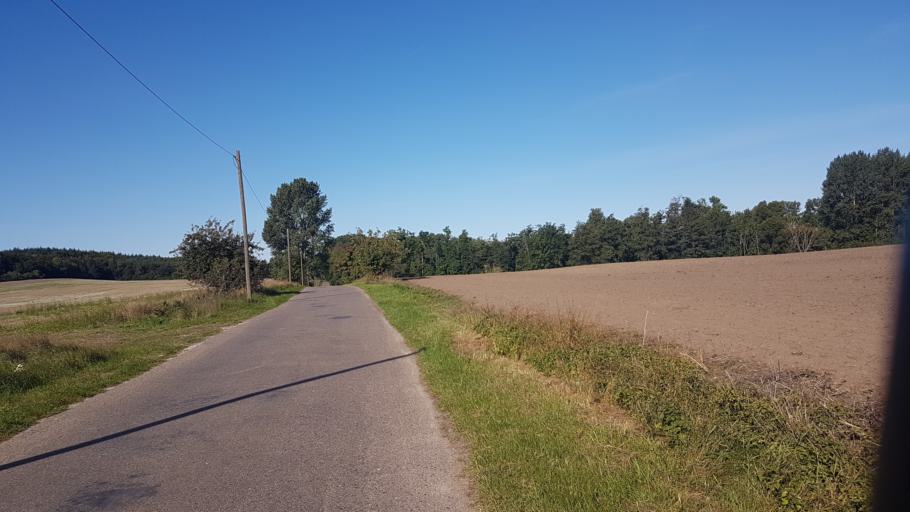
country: DE
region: Mecklenburg-Vorpommern
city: Sagard
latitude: 54.5048
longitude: 13.5247
